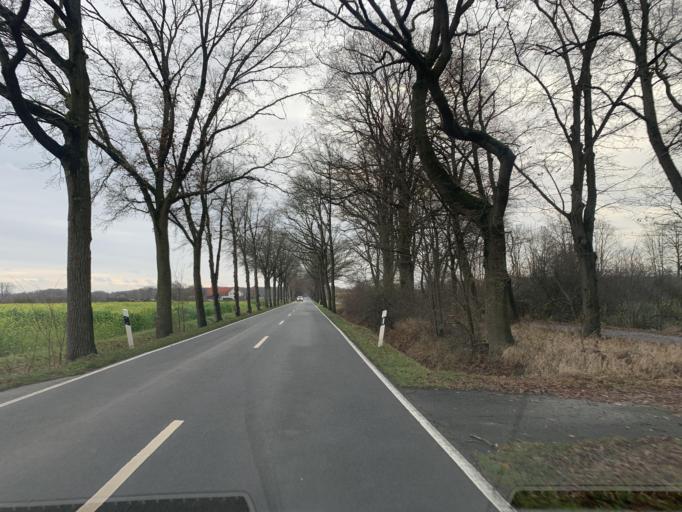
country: DE
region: North Rhine-Westphalia
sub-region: Regierungsbezirk Munster
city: Ascheberg
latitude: 51.8676
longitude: 7.6149
